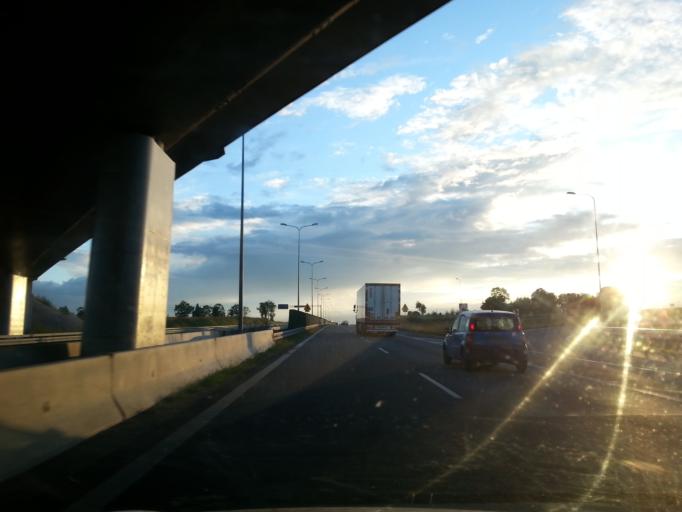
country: PL
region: Lower Silesian Voivodeship
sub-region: Powiat olesnicki
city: Sycow
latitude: 51.2955
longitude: 17.6798
